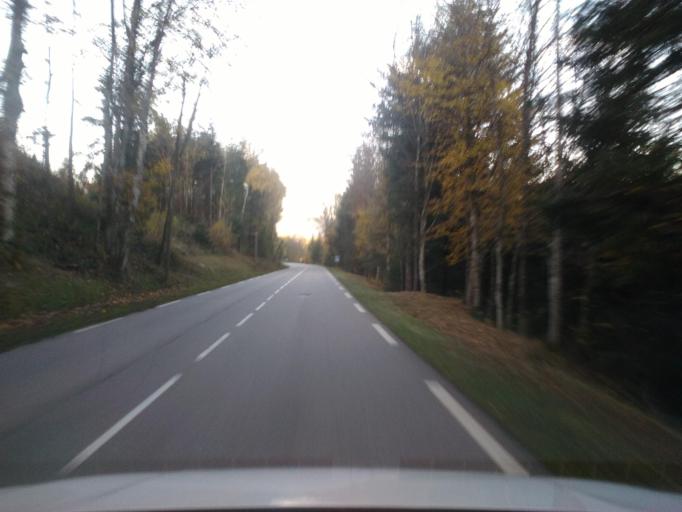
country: FR
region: Lorraine
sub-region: Departement des Vosges
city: Senones
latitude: 48.4083
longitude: 7.0621
